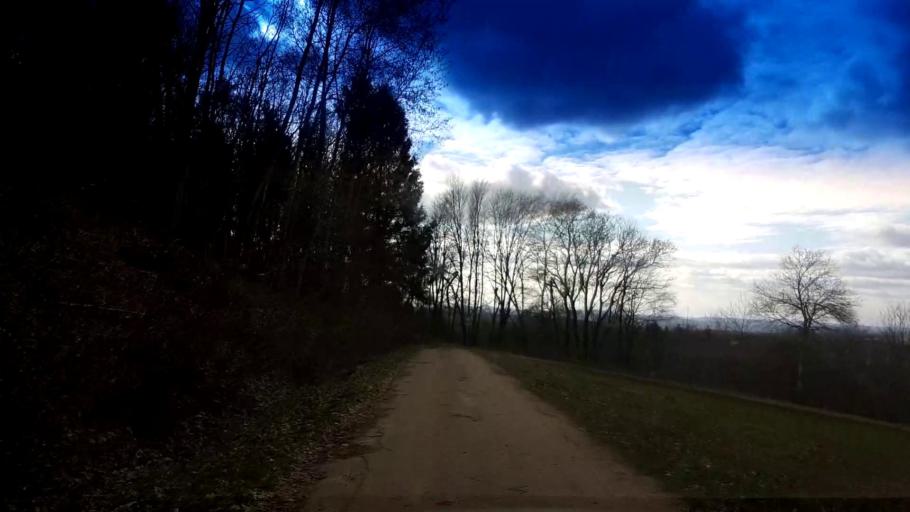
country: DE
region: Bavaria
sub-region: Upper Franconia
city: Schesslitz
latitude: 50.0089
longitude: 11.0363
